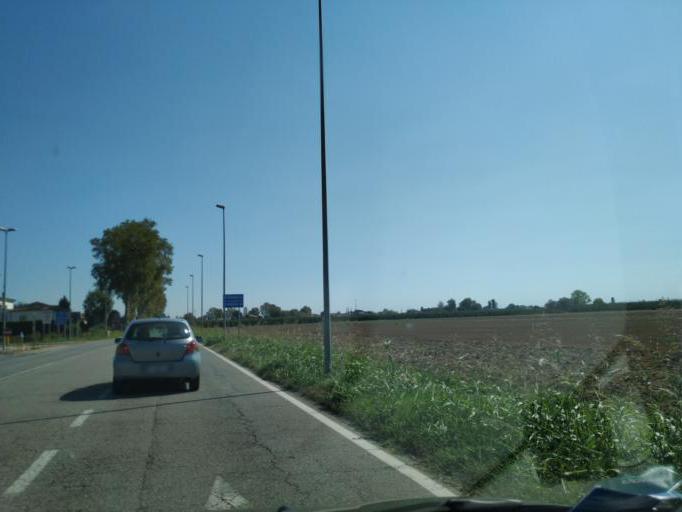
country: IT
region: Emilia-Romagna
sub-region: Provincia di Ferrara
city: La Saletta-Tamara
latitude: 44.8809
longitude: 11.7395
